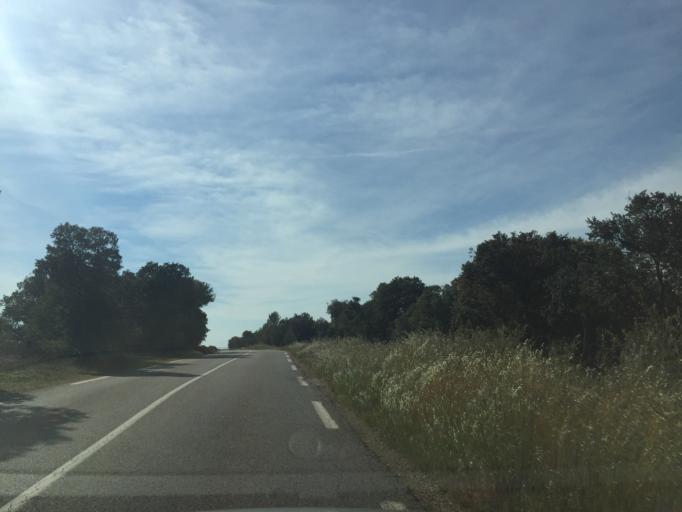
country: FR
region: Provence-Alpes-Cote d'Azur
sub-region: Departement du Var
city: Ginasservis
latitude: 43.6659
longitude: 5.8832
